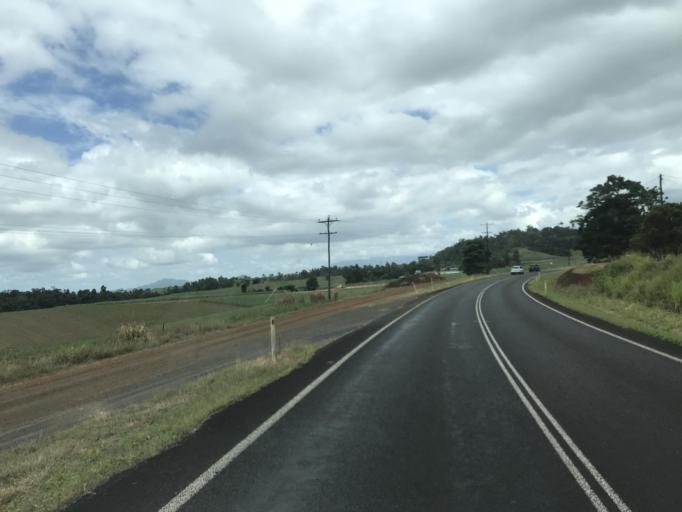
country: AU
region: Queensland
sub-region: Cassowary Coast
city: Innisfail
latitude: -17.5757
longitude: 145.9608
